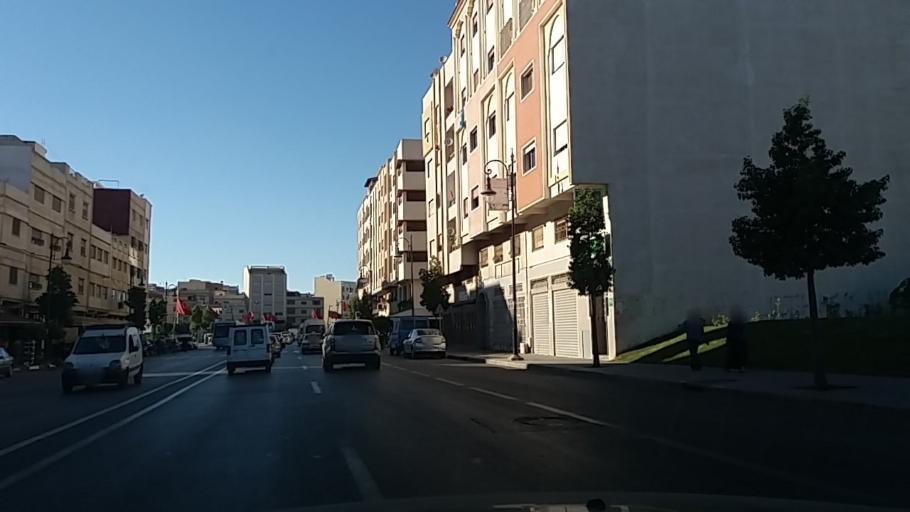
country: MA
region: Tanger-Tetouan
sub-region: Tanger-Assilah
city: Tangier
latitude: 35.7505
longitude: -5.7993
